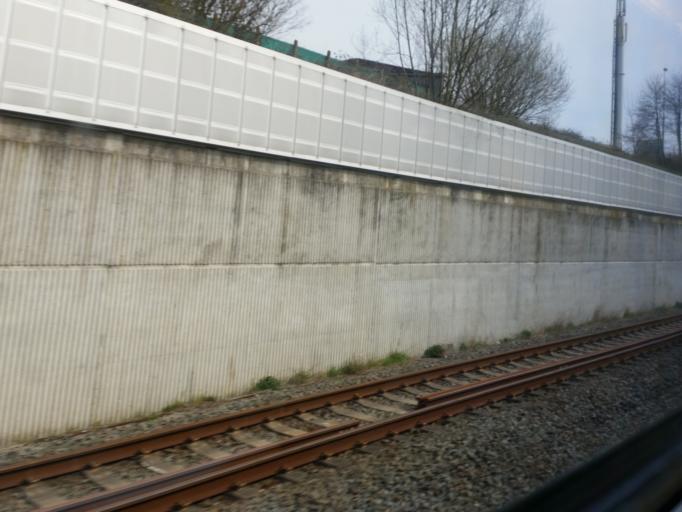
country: BE
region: Flanders
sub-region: Provincie Vlaams-Brabant
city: Ternat
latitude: 50.8734
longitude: 4.1312
